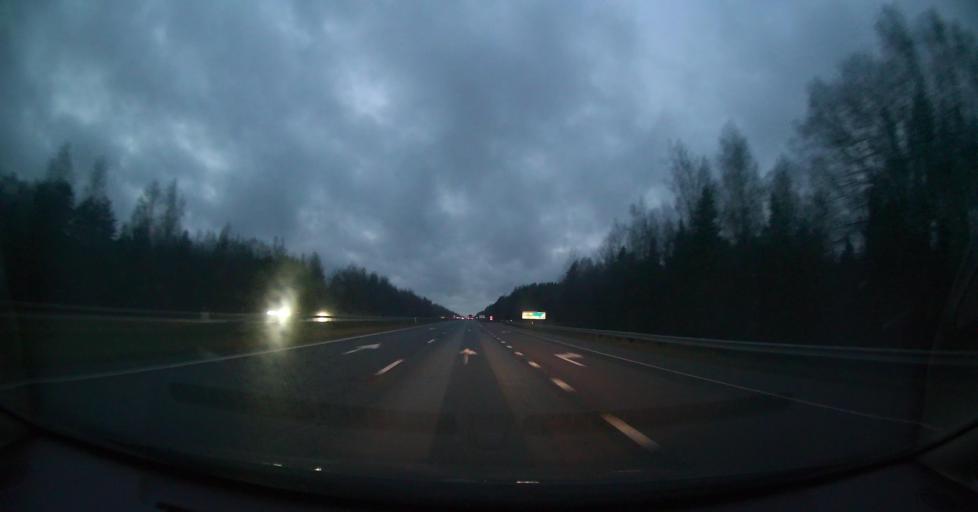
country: EE
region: Harju
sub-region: Kuusalu vald
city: Kuusalu
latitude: 59.4608
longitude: 25.6046
